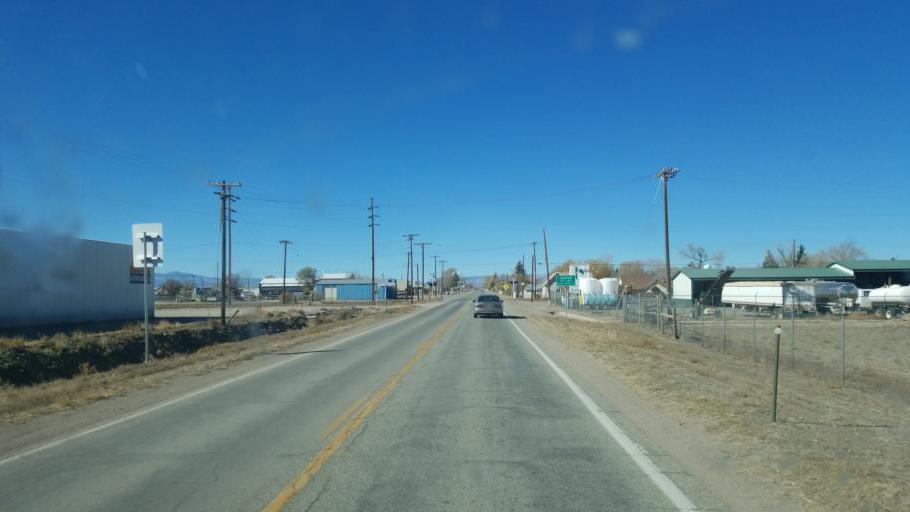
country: US
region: Colorado
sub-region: Saguache County
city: Center
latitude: 37.7483
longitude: -106.1016
